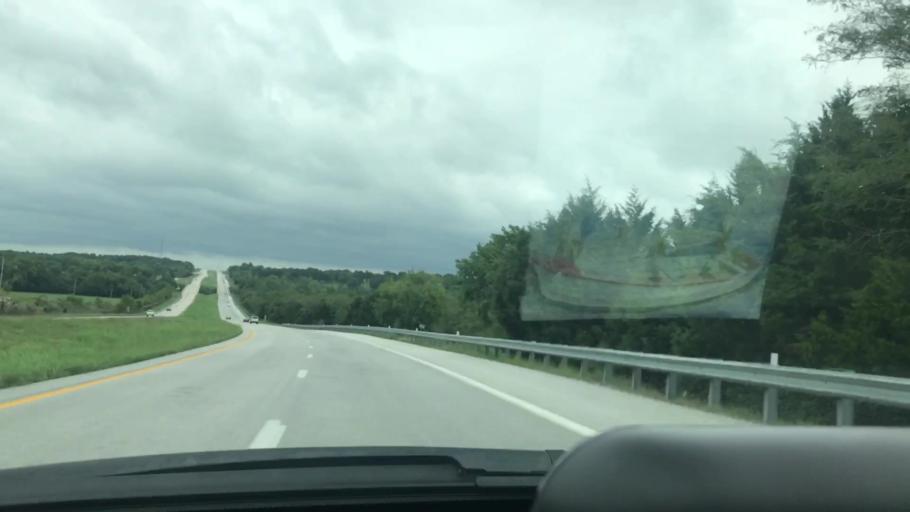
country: US
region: Missouri
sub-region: Greene County
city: Fair Grove
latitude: 37.4091
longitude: -93.1456
